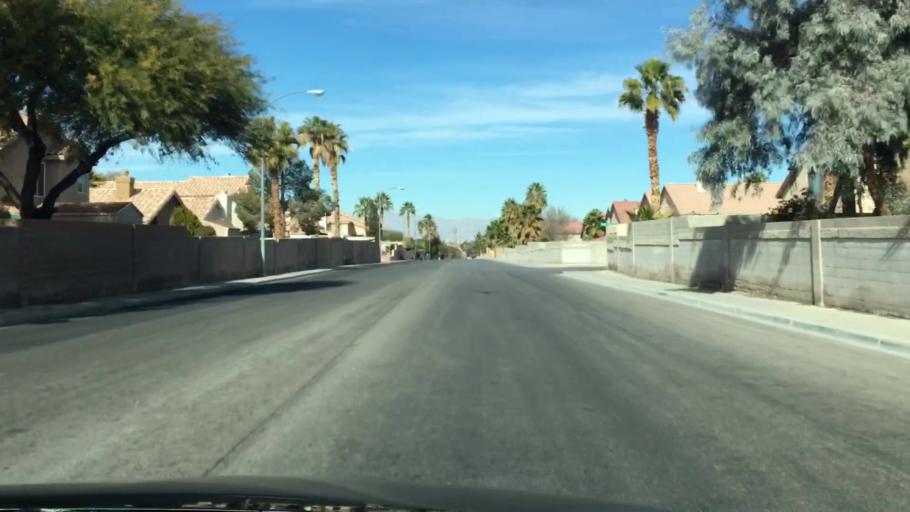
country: US
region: Nevada
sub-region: Clark County
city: Paradise
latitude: 36.0375
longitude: -115.1407
